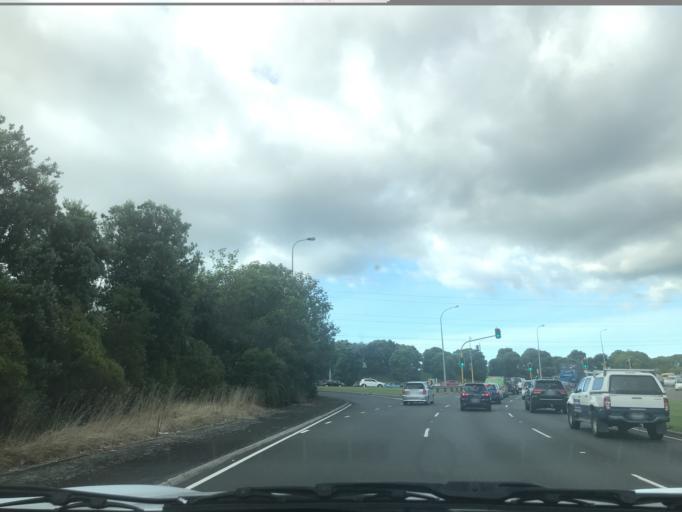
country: NZ
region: Auckland
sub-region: Auckland
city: Tamaki
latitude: -36.9116
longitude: 174.8528
